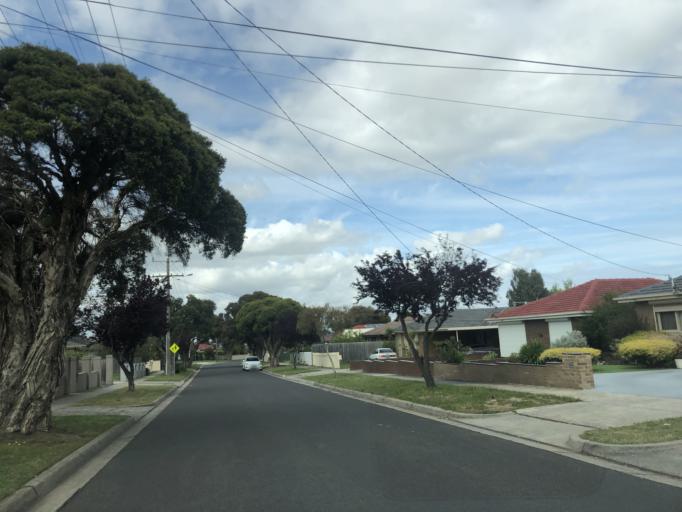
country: AU
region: Victoria
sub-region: Greater Dandenong
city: Dandenong North
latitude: -37.9552
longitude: 145.2150
